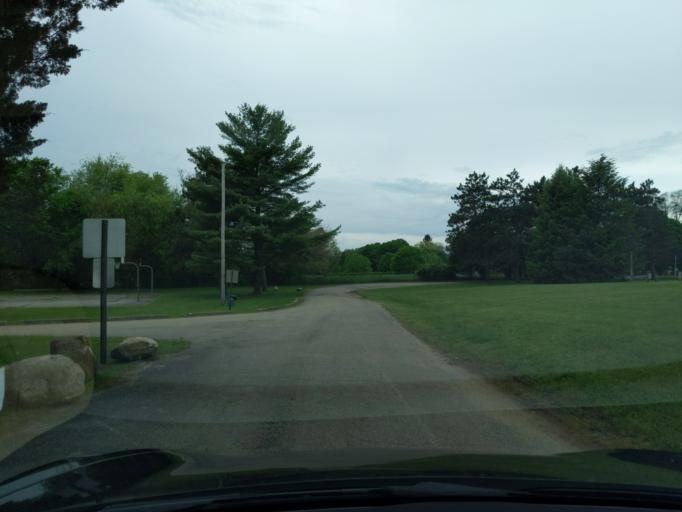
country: US
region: Michigan
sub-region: Ingham County
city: Leslie
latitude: 42.4007
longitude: -84.3467
